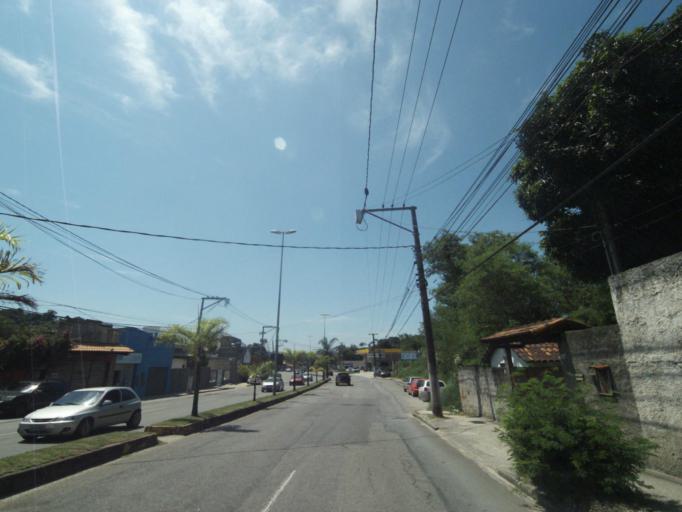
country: BR
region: Rio de Janeiro
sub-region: Sao Goncalo
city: Sao Goncalo
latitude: -22.8888
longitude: -43.0337
